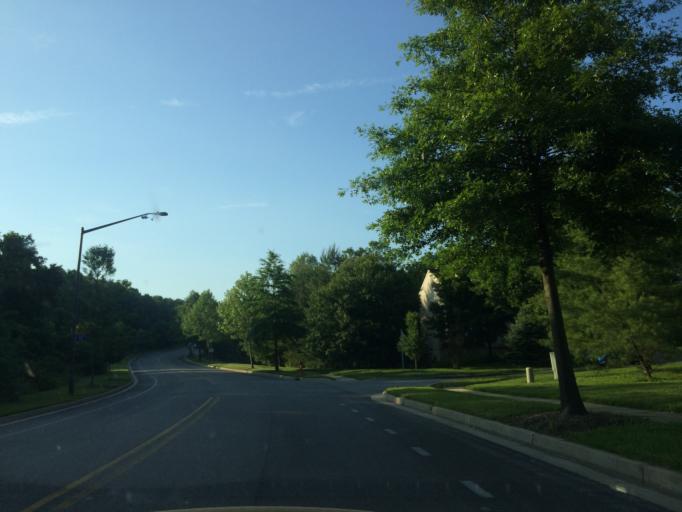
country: US
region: Maryland
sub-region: Howard County
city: Highland
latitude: 39.2002
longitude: -76.9259
